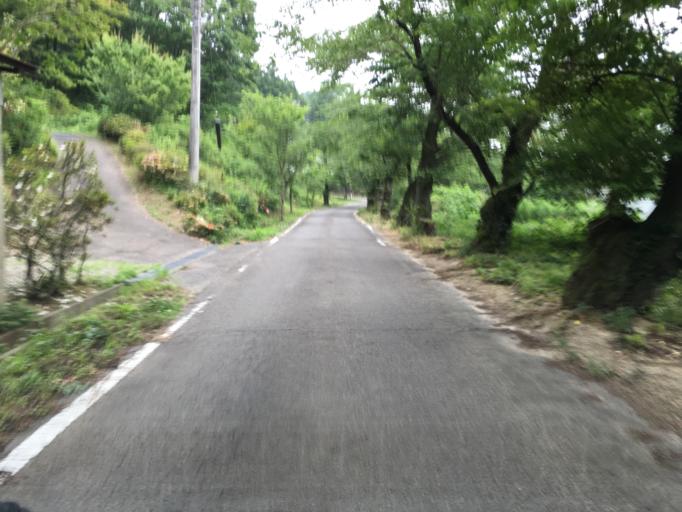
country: JP
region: Fukushima
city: Nihommatsu
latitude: 37.6465
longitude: 140.5291
